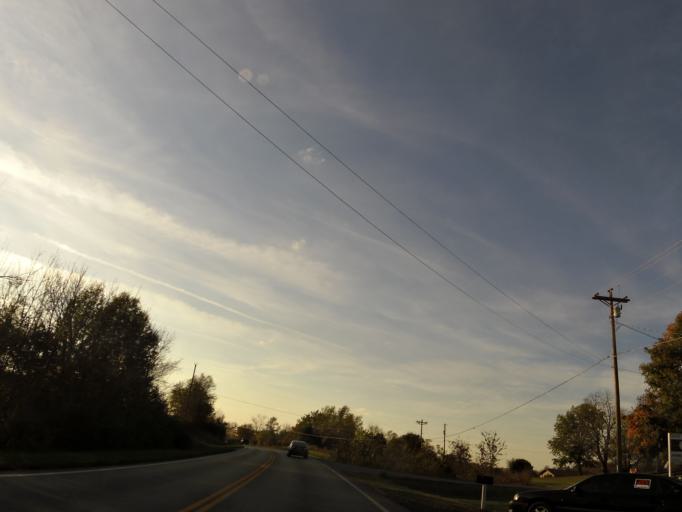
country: US
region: Kentucky
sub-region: Garrard County
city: Lancaster
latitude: 37.6733
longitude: -84.6384
